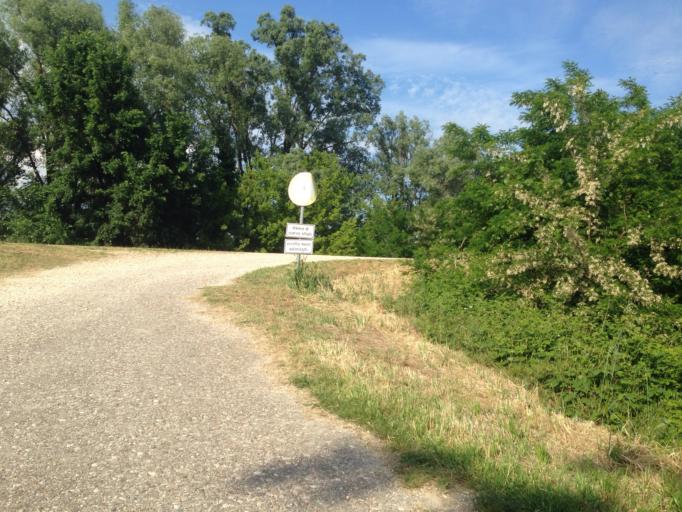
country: IT
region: Veneto
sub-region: Provincia di Verona
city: Zevio
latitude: 45.3724
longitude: 11.1522
